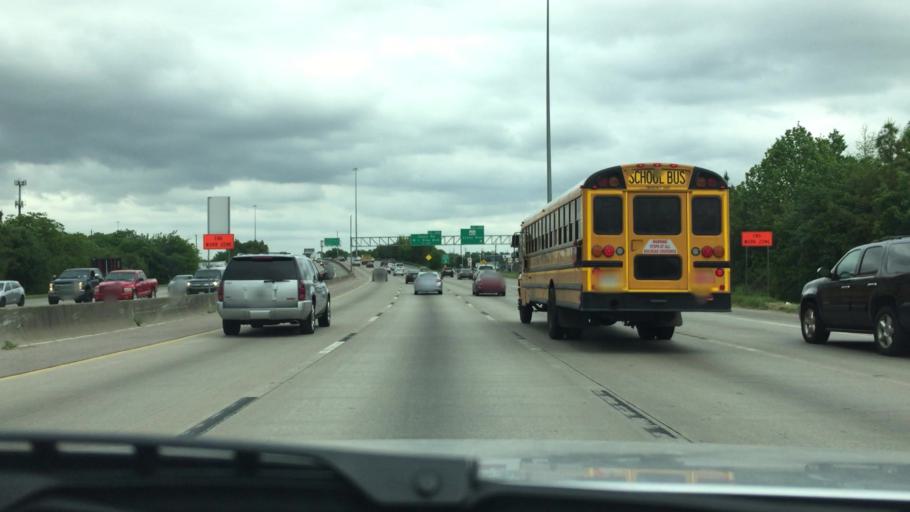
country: US
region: Texas
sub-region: Harris County
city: Southside Place
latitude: 29.6802
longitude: -95.3605
